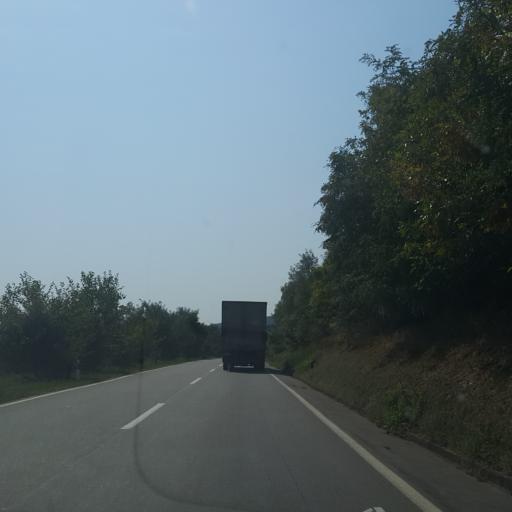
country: RS
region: Central Serbia
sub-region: Zajecarski Okrug
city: Zajecar
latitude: 43.8269
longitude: 22.2882
